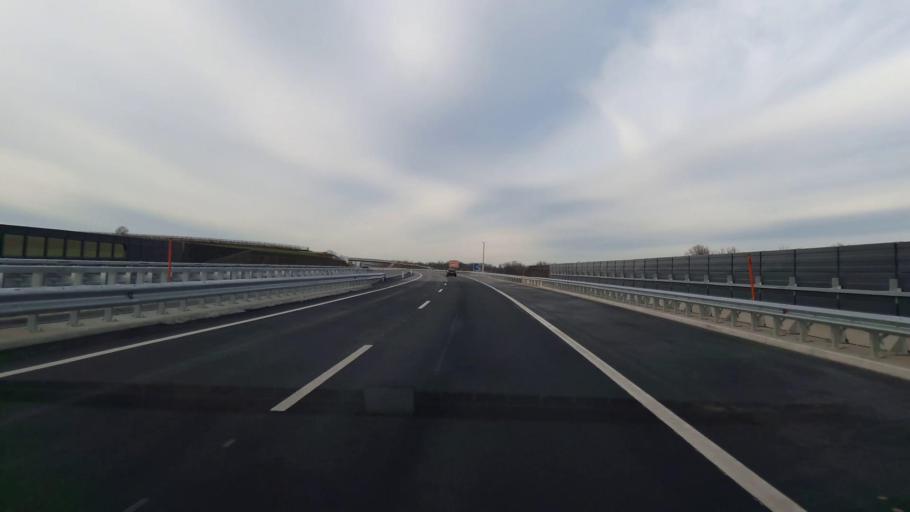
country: AT
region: Lower Austria
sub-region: Politischer Bezirk Mistelbach
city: Herrnbaumgarten
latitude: 48.6602
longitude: 16.6880
